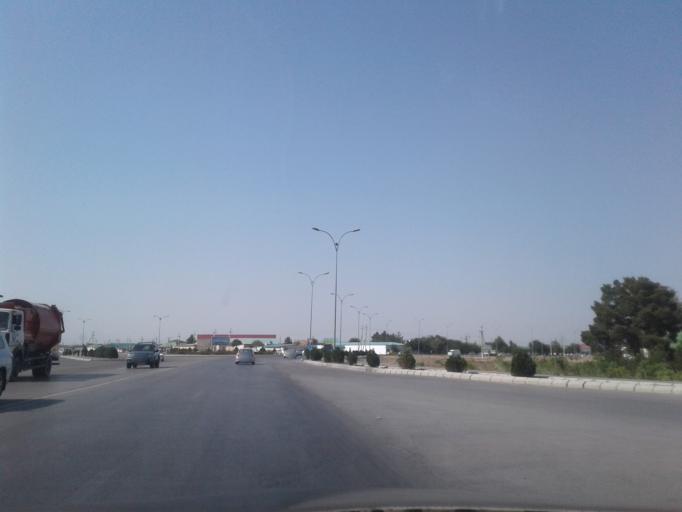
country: TM
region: Ahal
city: Ashgabat
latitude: 37.9682
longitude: 58.4227
